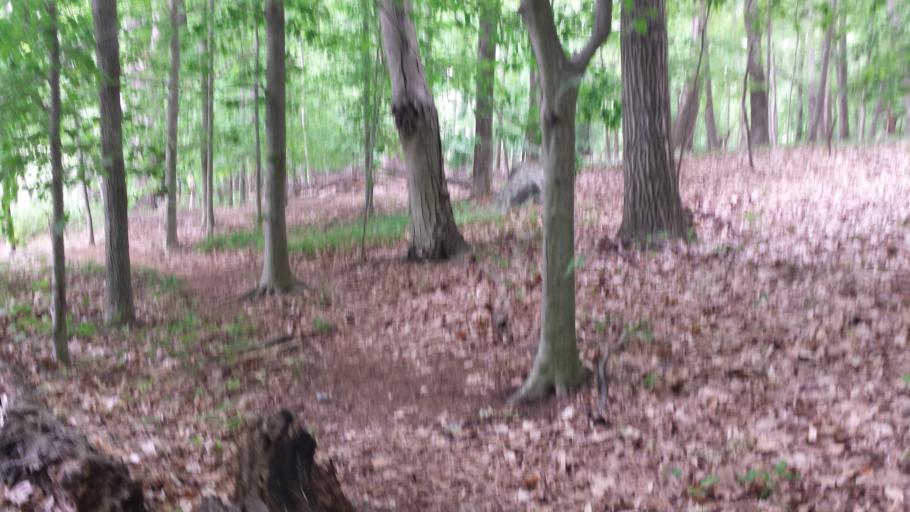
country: US
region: New York
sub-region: Putnam County
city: Peach Lake
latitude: 41.3109
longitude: -73.5693
